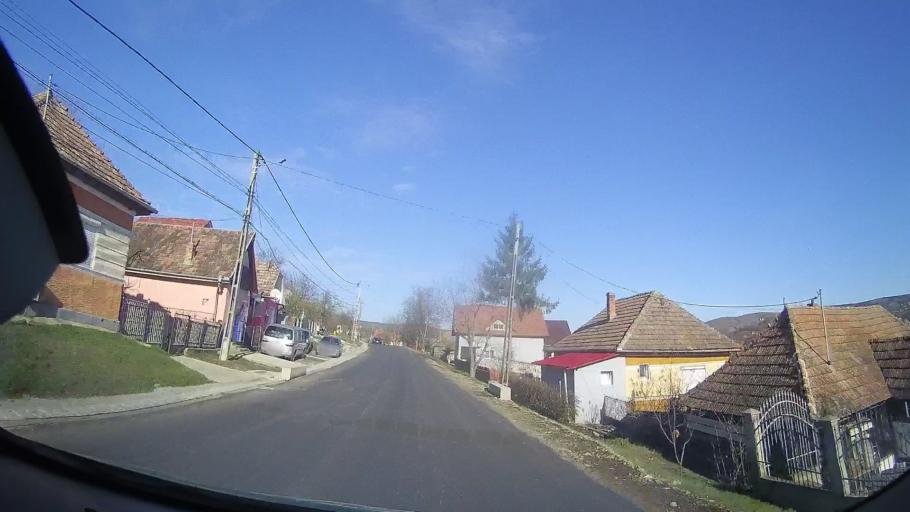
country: RO
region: Mures
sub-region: Comuna Zau De Campie
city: Zau de Campie
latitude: 46.6115
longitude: 24.1235
